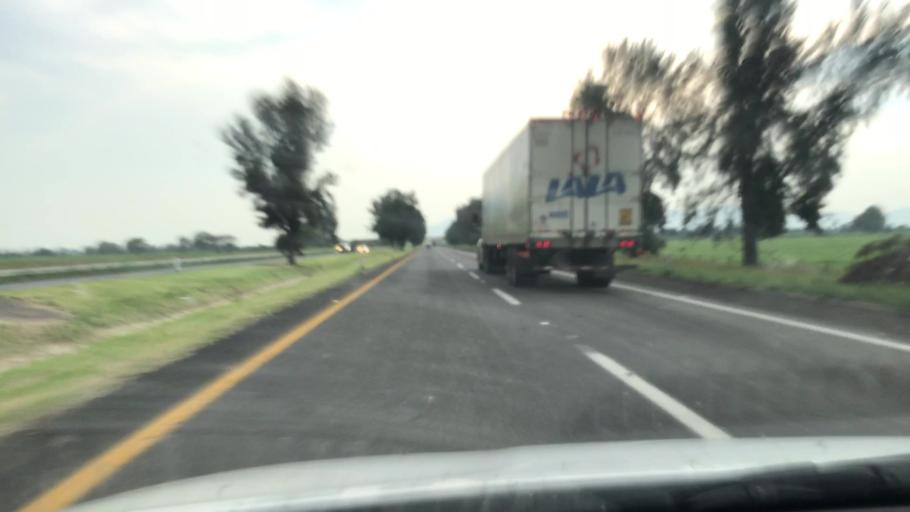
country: MX
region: Michoacan
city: Vistahermosa de Negrete
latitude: 20.2989
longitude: -102.4809
